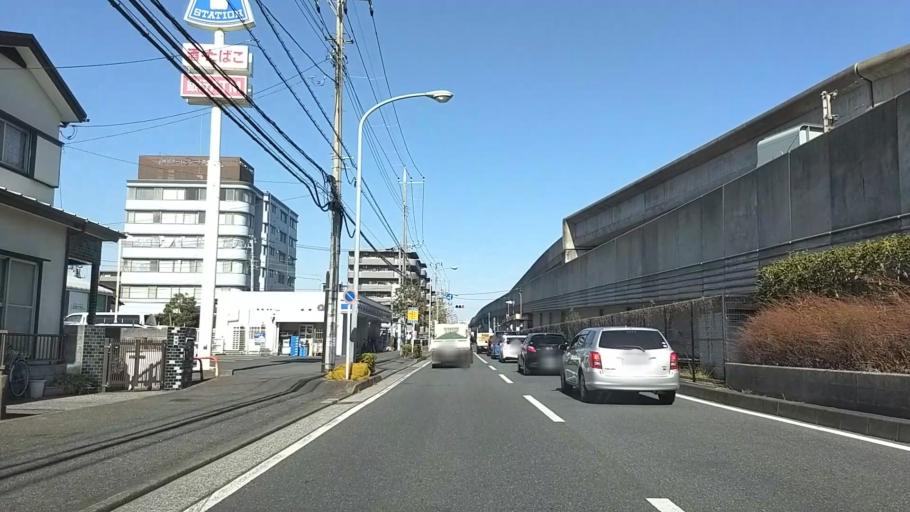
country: JP
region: Kanagawa
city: Yokohama
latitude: 35.5221
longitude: 139.6124
